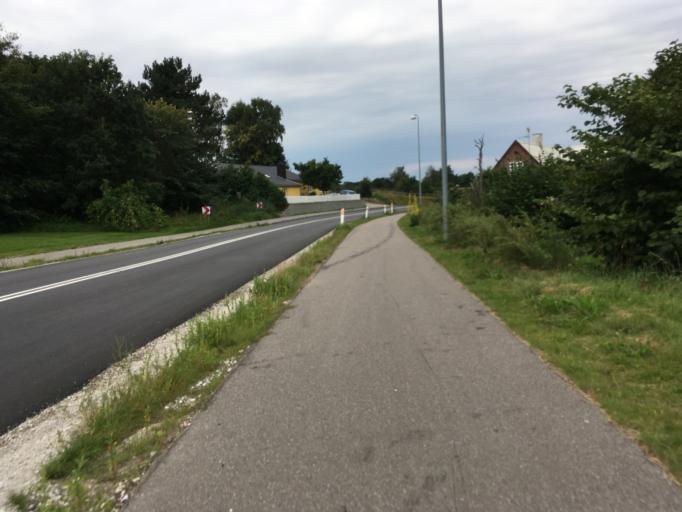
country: DK
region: Capital Region
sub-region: Hillerod Kommune
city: Hillerod
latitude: 55.9265
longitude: 12.2452
